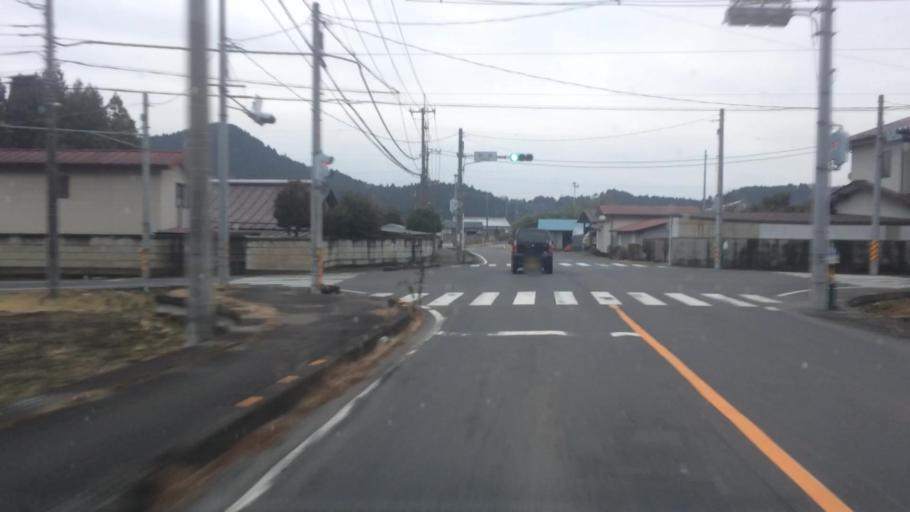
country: JP
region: Tochigi
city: Imaichi
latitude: 36.7407
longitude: 139.7485
